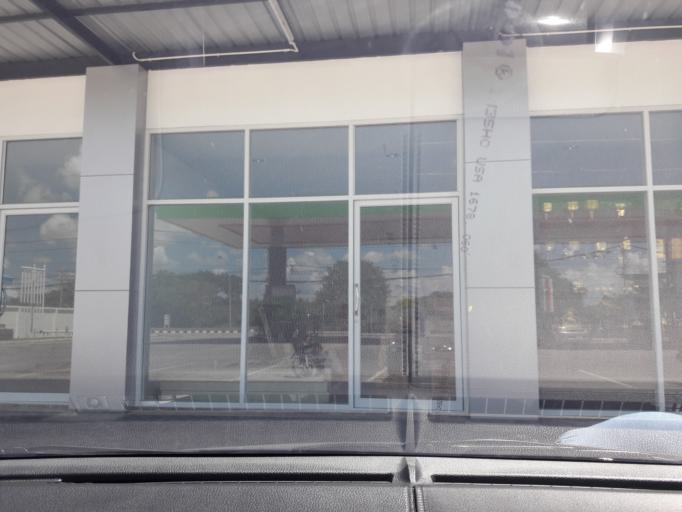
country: TH
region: Kanchanaburi
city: Tha Maka
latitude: 14.0354
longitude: 99.8025
